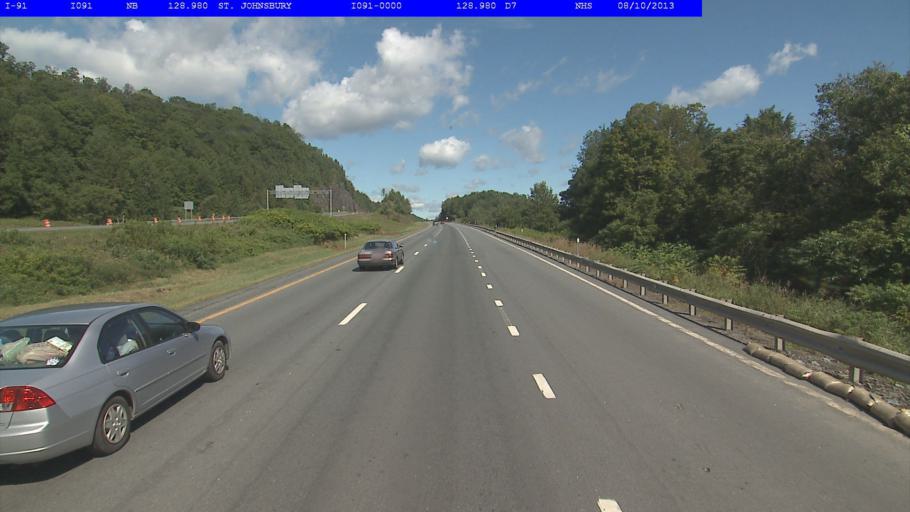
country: US
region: Vermont
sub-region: Caledonia County
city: Saint Johnsbury
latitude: 44.4061
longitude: -72.0234
